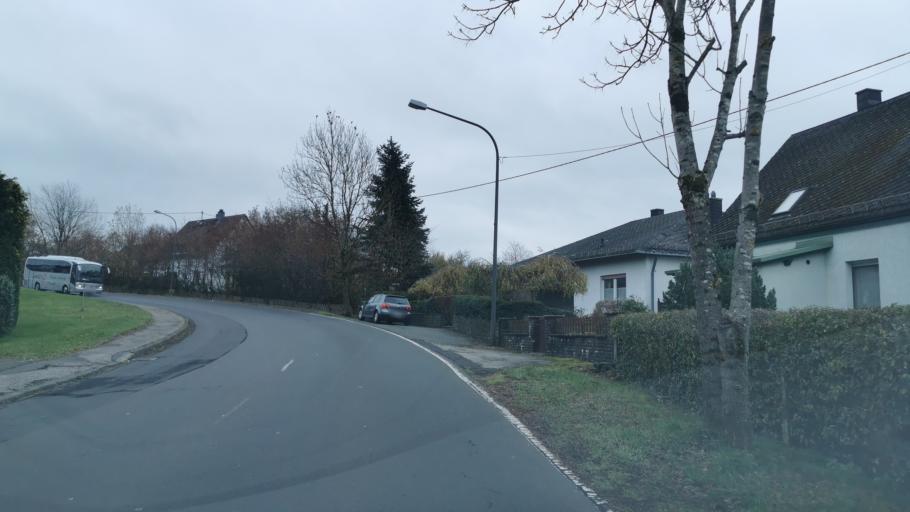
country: DE
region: Rheinland-Pfalz
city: Darscheid
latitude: 50.2109
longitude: 6.8867
